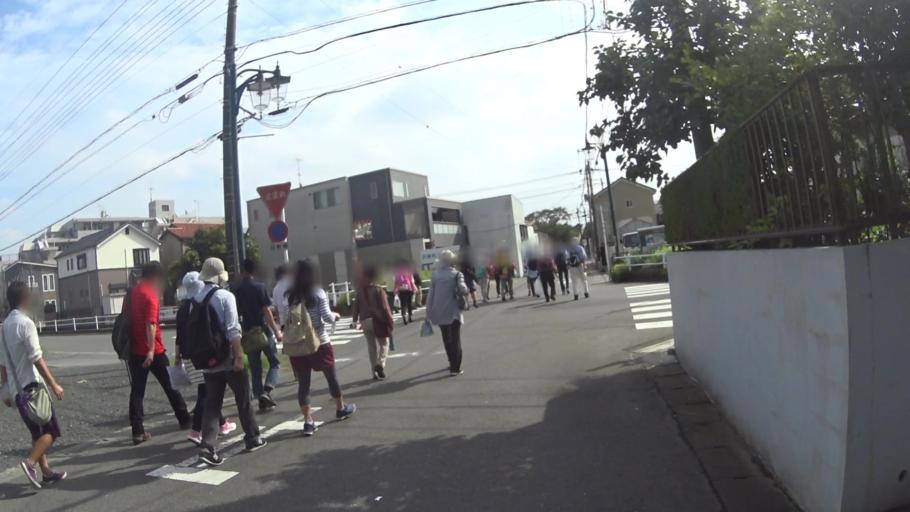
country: JP
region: Saitama
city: Iwatsuki
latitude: 35.9671
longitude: 139.7096
